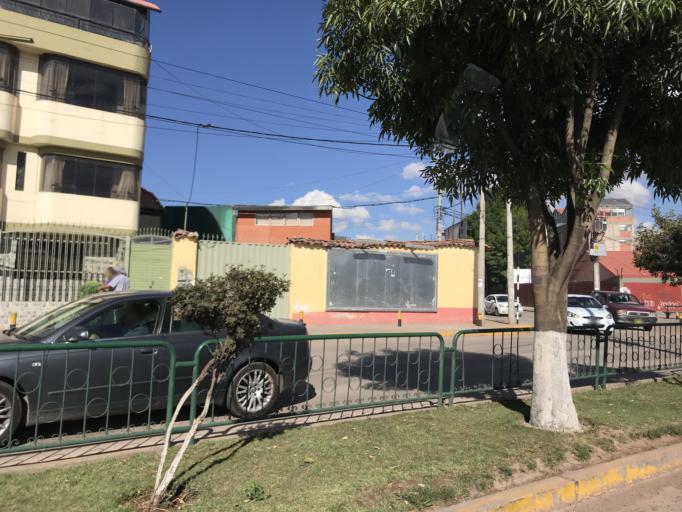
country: PE
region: Cusco
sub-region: Provincia de Cusco
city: Cusco
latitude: -13.5362
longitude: -71.9554
